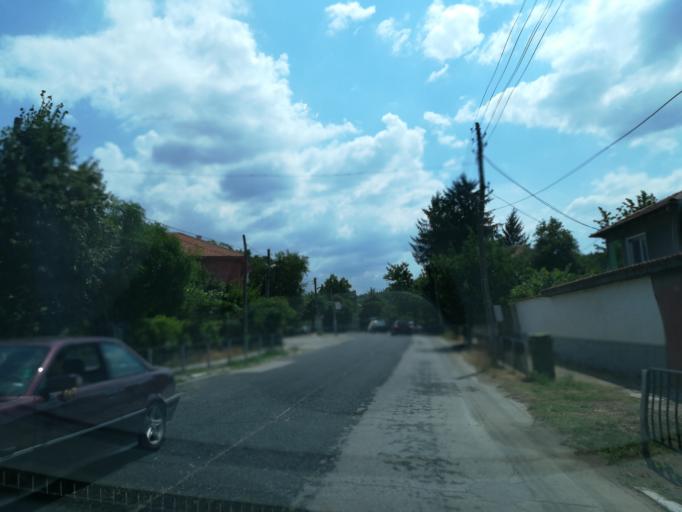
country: BG
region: Plovdiv
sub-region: Obshtina Asenovgrad
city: Asenovgrad
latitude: 41.9327
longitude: 24.9818
